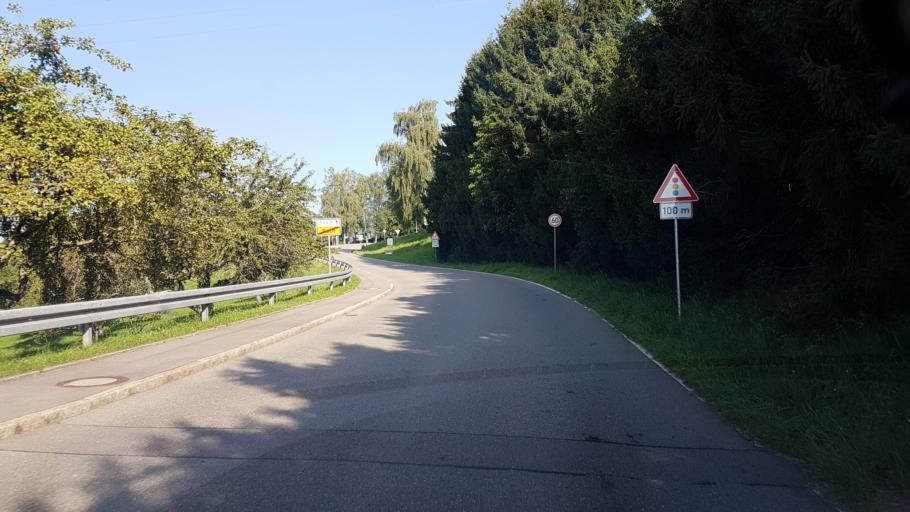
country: DE
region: Baden-Wuerttemberg
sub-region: Freiburg Region
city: Albbruck
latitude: 47.6148
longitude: 8.1096
